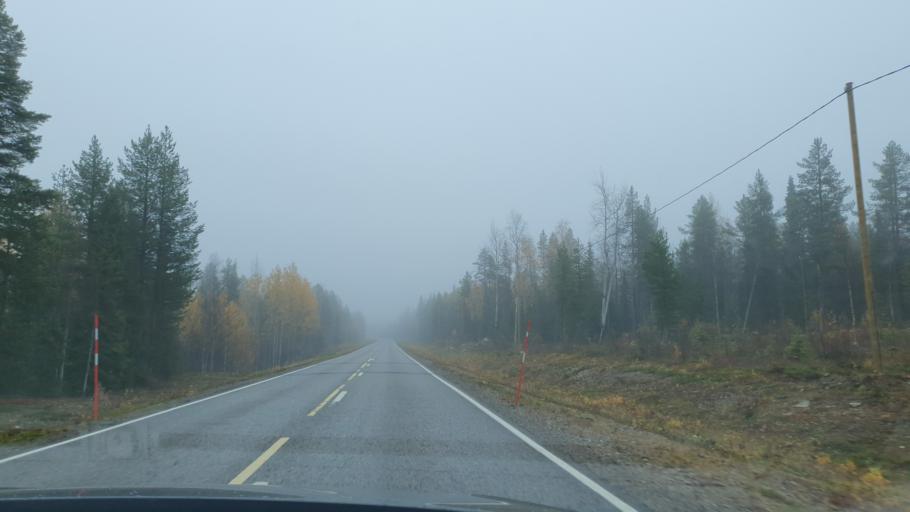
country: FI
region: Lapland
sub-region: Tunturi-Lappi
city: Kittilae
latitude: 67.6619
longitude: 24.8127
